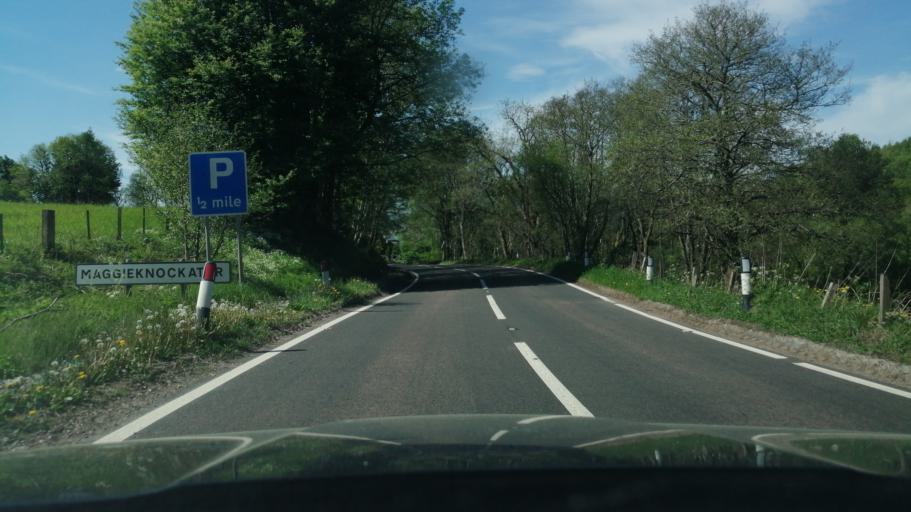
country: GB
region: Scotland
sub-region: Moray
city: Dufftown
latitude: 57.4999
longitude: -3.1374
